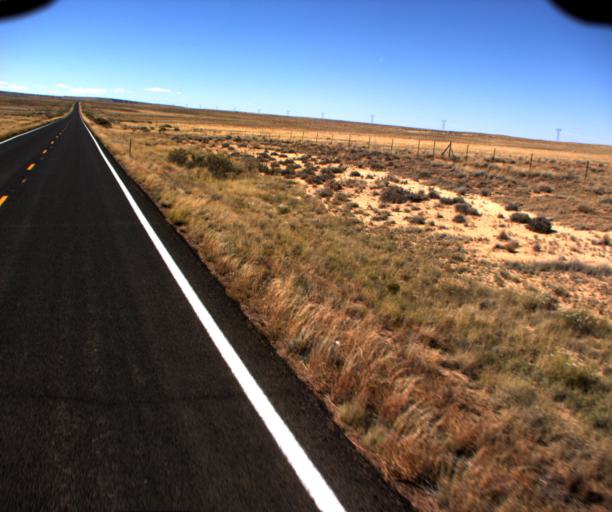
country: US
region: Arizona
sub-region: Navajo County
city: First Mesa
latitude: 35.9724
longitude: -110.7818
